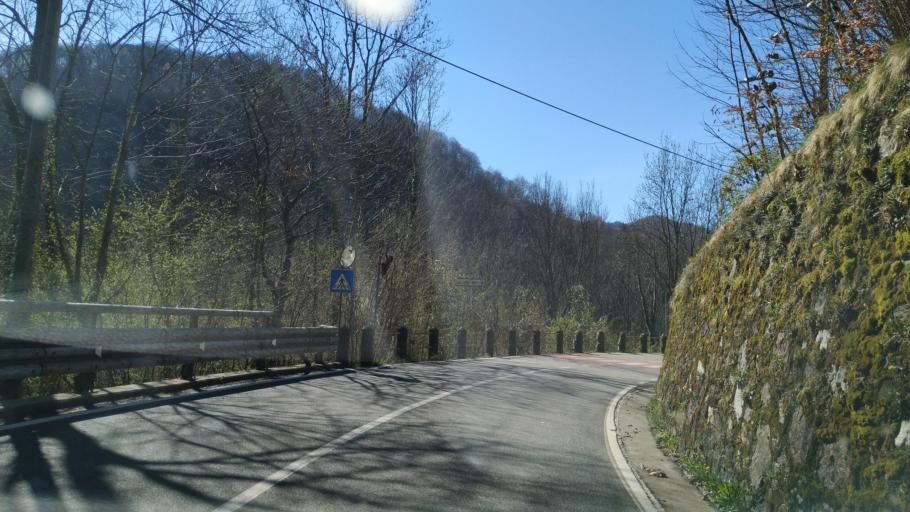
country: IT
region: Piedmont
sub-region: Provincia di Vercelli
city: Civiasco
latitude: 45.8117
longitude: 8.3031
